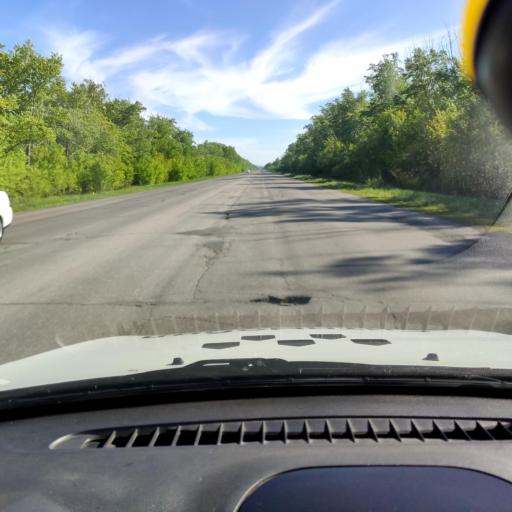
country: RU
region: Samara
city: Tol'yatti
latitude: 53.6175
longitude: 49.4136
